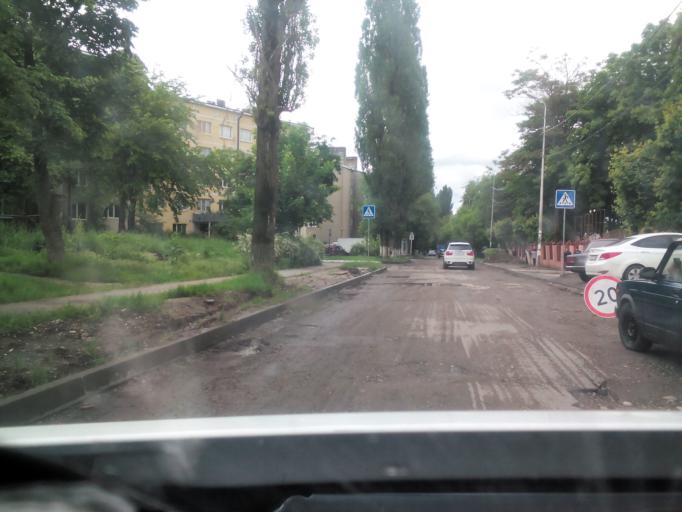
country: RU
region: Stavropol'skiy
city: Pyatigorsk
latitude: 44.0514
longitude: 43.0578
